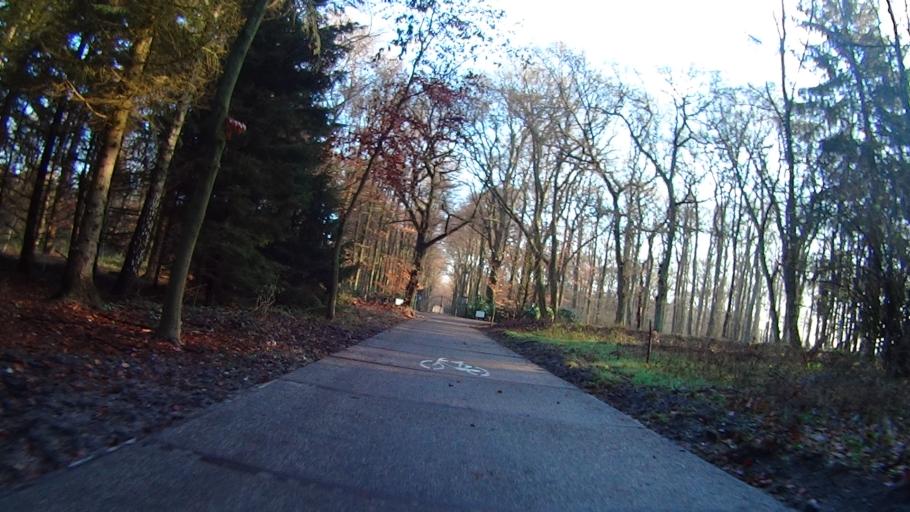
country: NL
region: Utrecht
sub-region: Gemeente Soest
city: Soest
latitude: 52.1397
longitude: 5.2753
